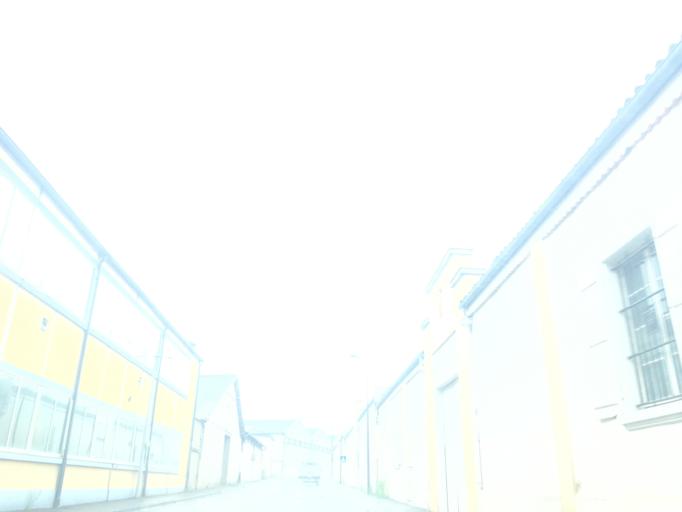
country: FR
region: Poitou-Charentes
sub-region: Departement de la Charente
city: Cognac
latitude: 45.6879
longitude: -0.3199
